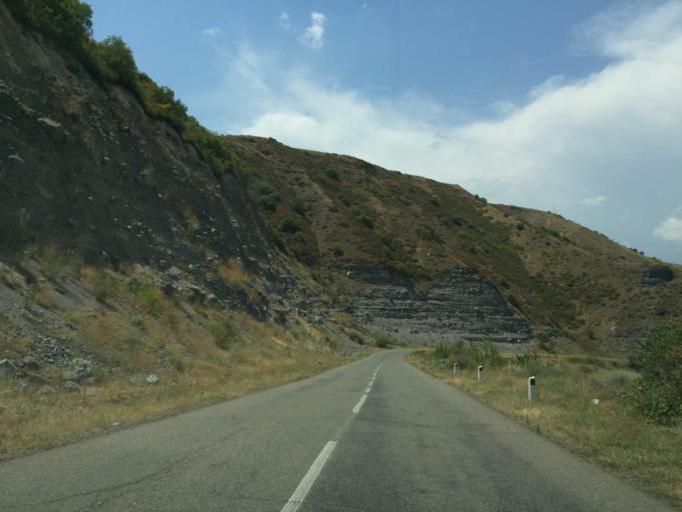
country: AZ
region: Lacin
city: Lacin
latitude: 39.5789
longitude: 46.5432
